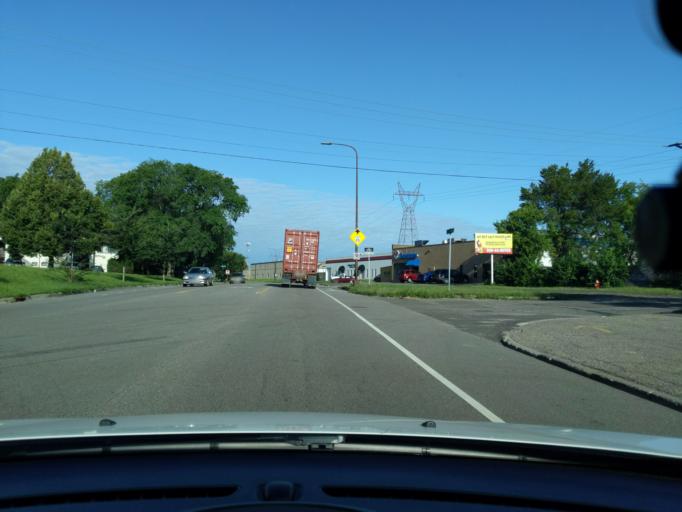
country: US
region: Minnesota
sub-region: Ramsey County
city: Falcon Heights
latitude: 44.9673
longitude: -93.1515
